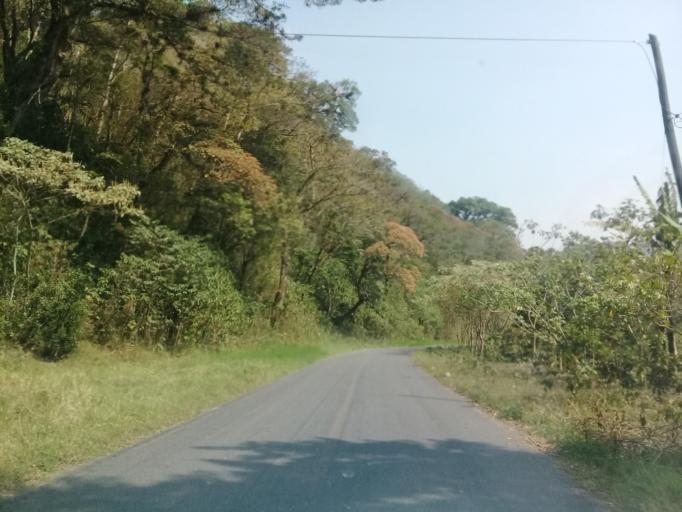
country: MX
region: Veracruz
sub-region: Ixtaczoquitlan
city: Campo Chico
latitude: 18.8329
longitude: -97.0145
